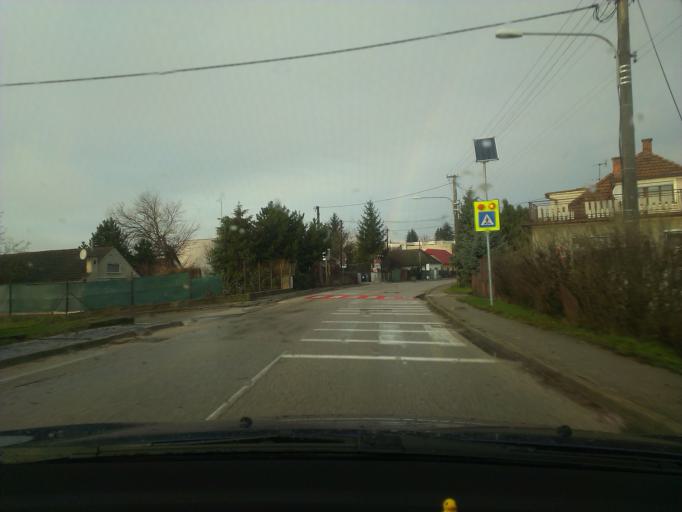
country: SK
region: Trnavsky
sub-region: Okres Trnava
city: Piestany
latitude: 48.6005
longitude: 17.8613
